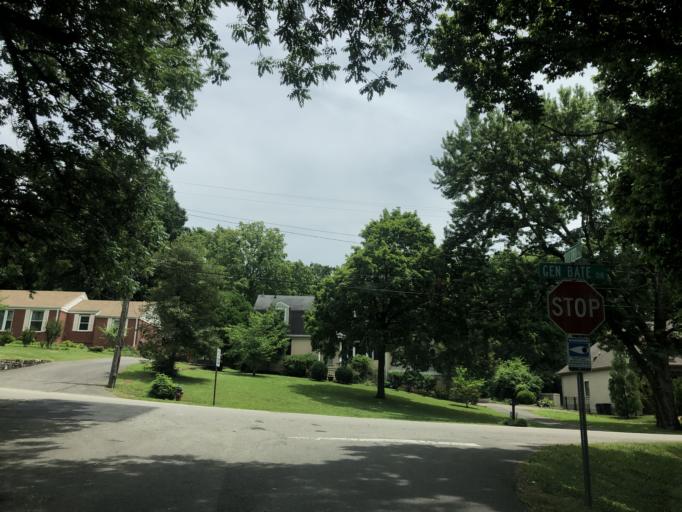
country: US
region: Tennessee
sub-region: Davidson County
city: Oak Hill
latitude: 36.1026
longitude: -86.7861
